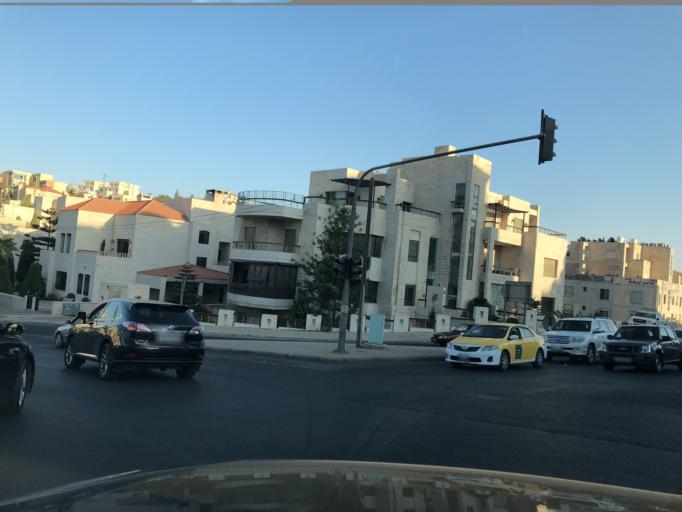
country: JO
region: Amman
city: Wadi as Sir
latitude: 31.9428
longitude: 35.8699
